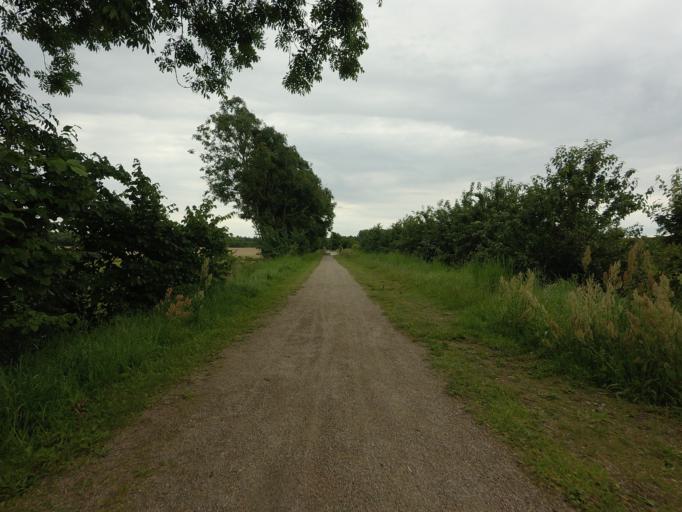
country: DK
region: North Denmark
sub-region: Alborg Kommune
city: Vadum
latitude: 57.1191
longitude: 9.8677
